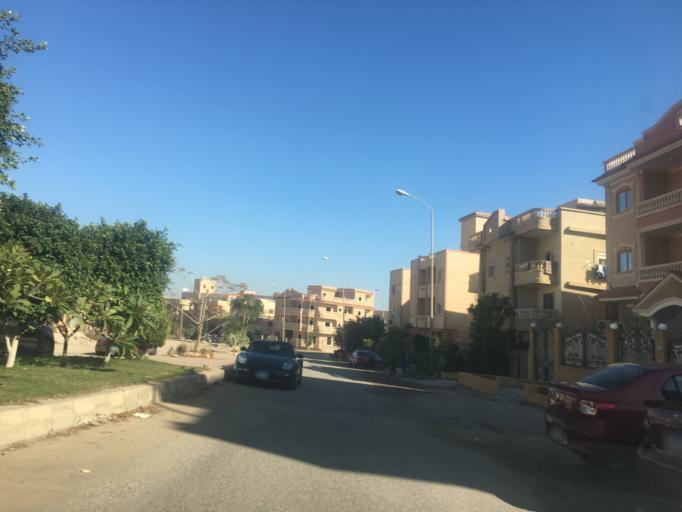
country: EG
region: Al Jizah
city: Awsim
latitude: 30.0264
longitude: 30.9828
